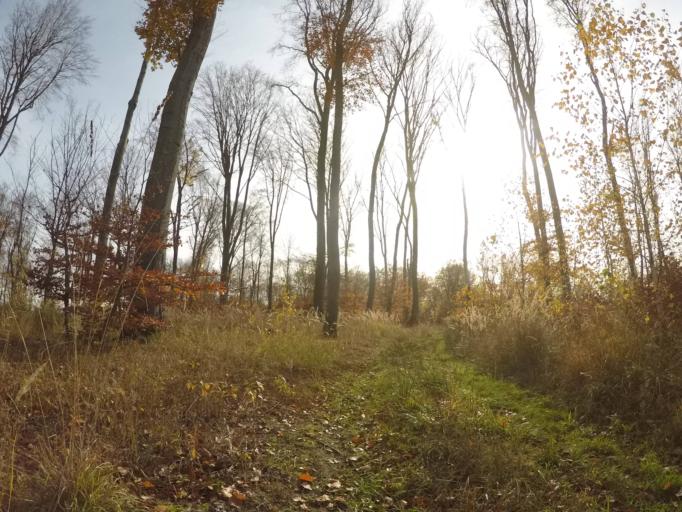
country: SK
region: Presovsky
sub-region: Okres Presov
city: Presov
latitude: 48.9507
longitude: 21.1868
